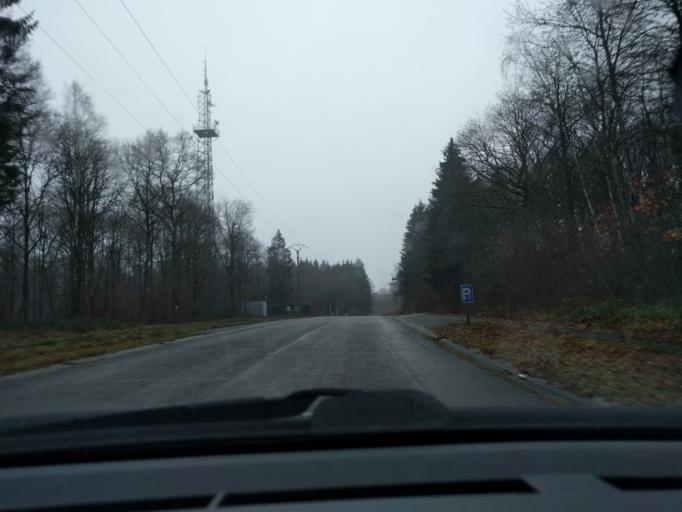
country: BE
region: Wallonia
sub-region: Province de Namur
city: Couvin
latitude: 50.0422
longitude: 4.5350
